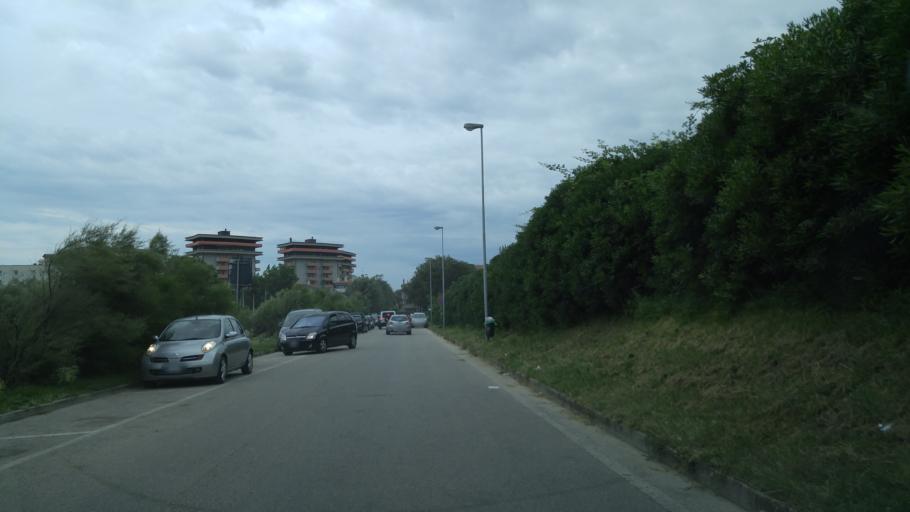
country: IT
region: The Marches
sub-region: Provincia di Pesaro e Urbino
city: Pesaro
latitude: 43.9218
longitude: 12.8948
